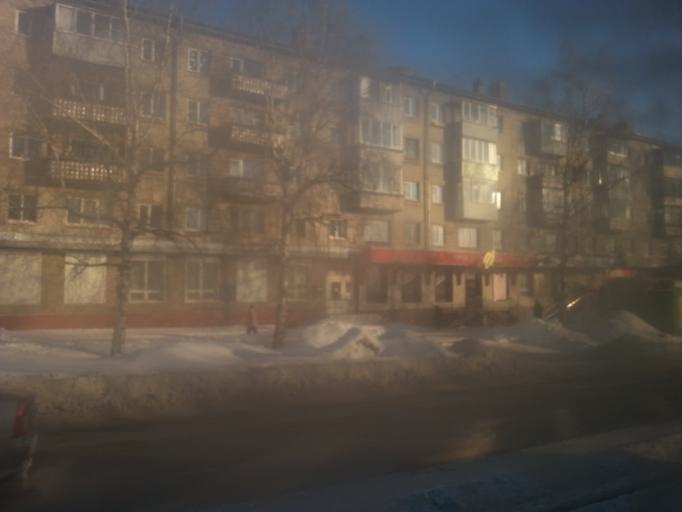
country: RU
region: Altai Krai
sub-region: Gorod Barnaulskiy
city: Barnaul
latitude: 53.3561
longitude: 83.7136
